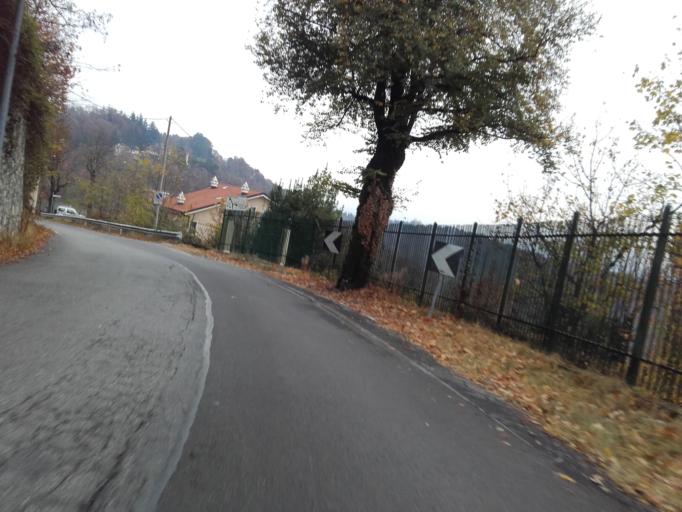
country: IT
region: Piedmont
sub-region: Provincia di Torino
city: San Mauro Torinese
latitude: 45.0780
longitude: 7.7681
